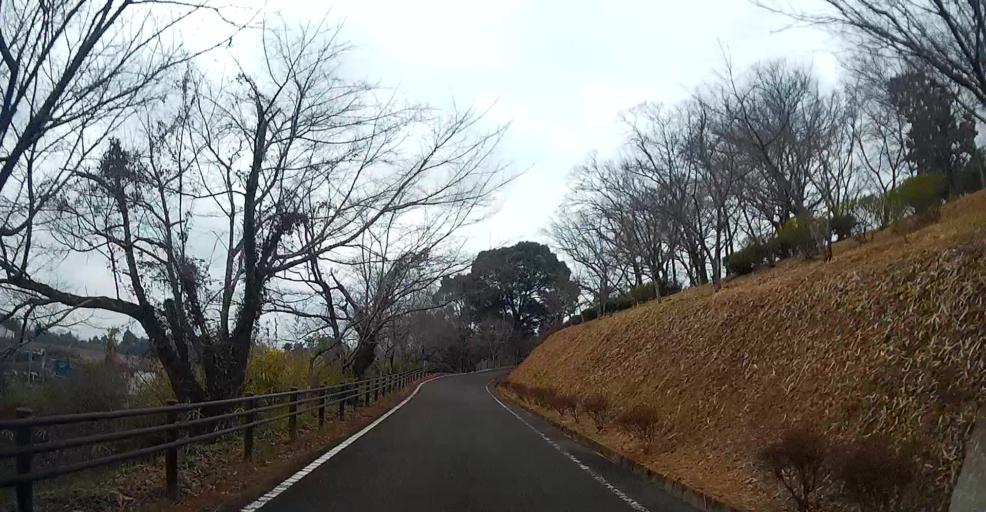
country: JP
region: Kumamoto
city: Matsubase
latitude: 32.6447
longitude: 130.7382
